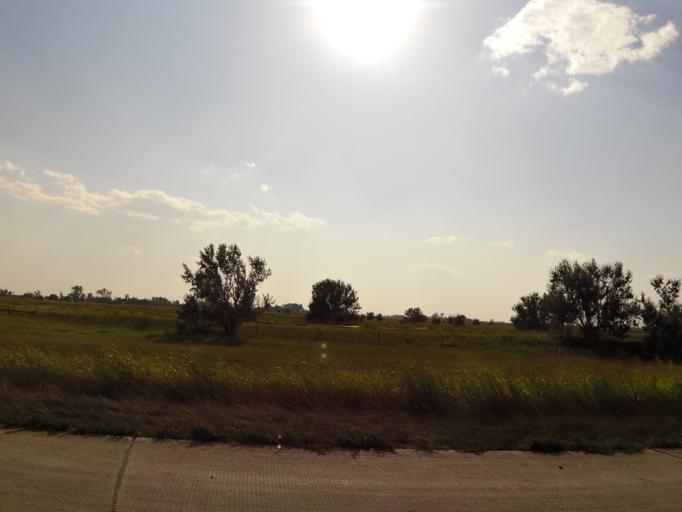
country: US
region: North Dakota
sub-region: Grand Forks County
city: Grand Forks
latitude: 48.0112
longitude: -97.1175
